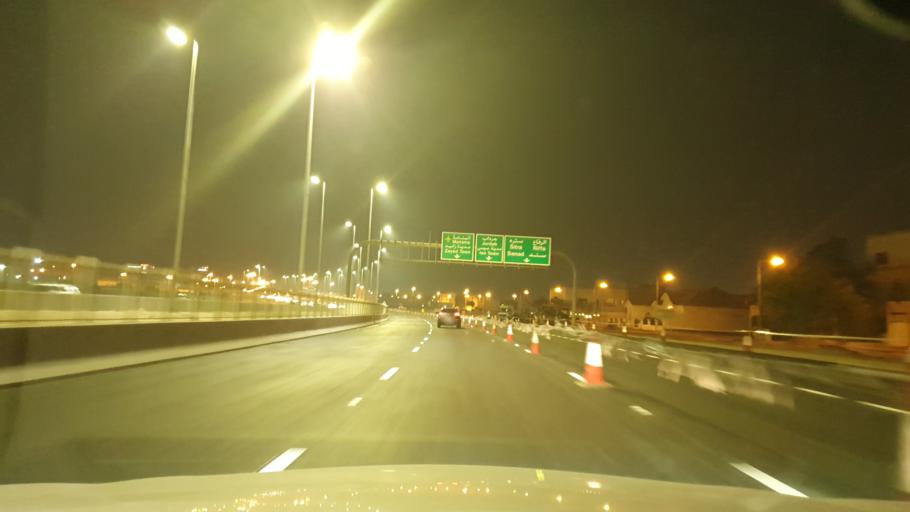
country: BH
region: Northern
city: Madinat `Isa
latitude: 26.1581
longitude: 50.5570
